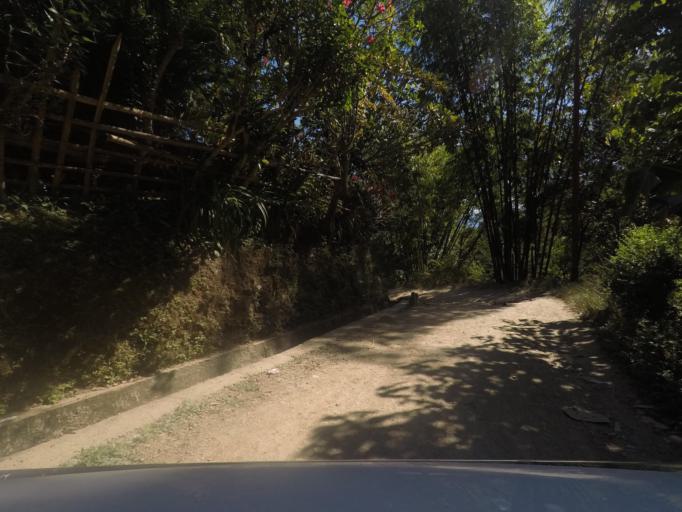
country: TL
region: Ermera
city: Gleno
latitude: -8.7294
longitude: 125.3395
